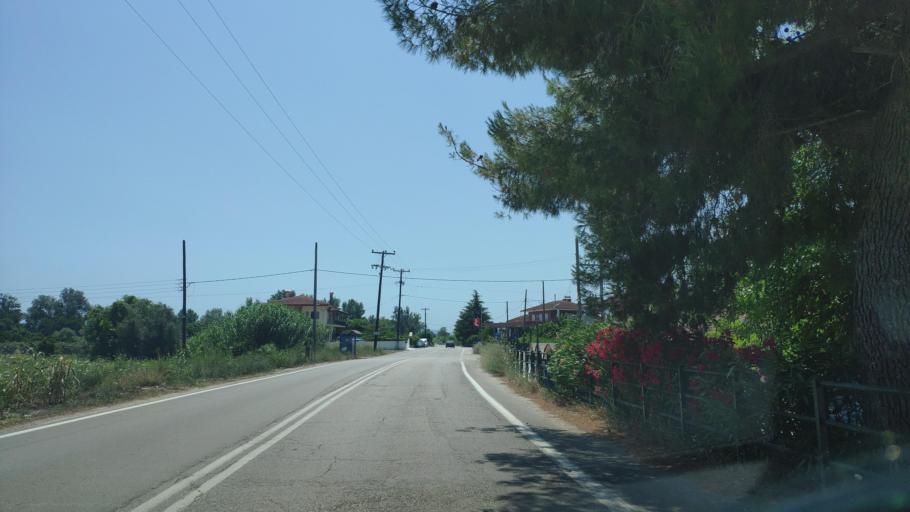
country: GR
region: Epirus
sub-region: Nomos Artas
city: Neochori
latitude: 39.0838
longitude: 21.0177
